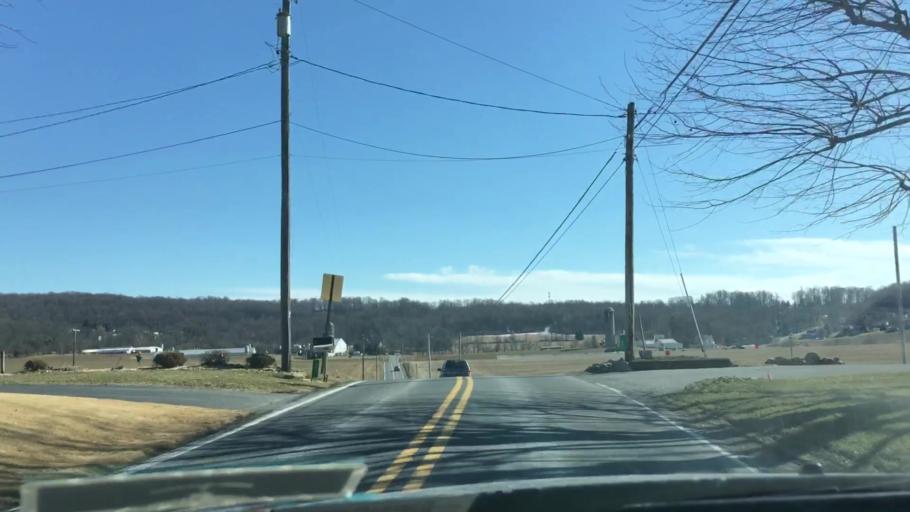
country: US
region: Pennsylvania
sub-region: Lancaster County
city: Reamstown
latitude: 40.1973
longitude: -76.1399
